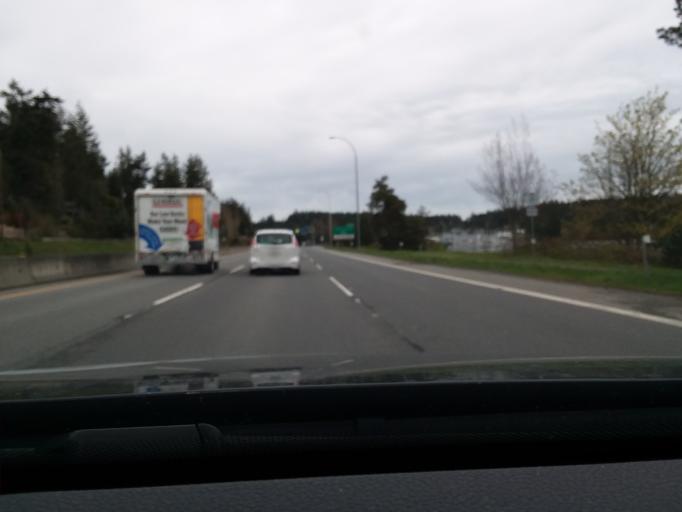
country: CA
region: British Columbia
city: North Saanich
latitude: 48.6776
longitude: -123.4237
